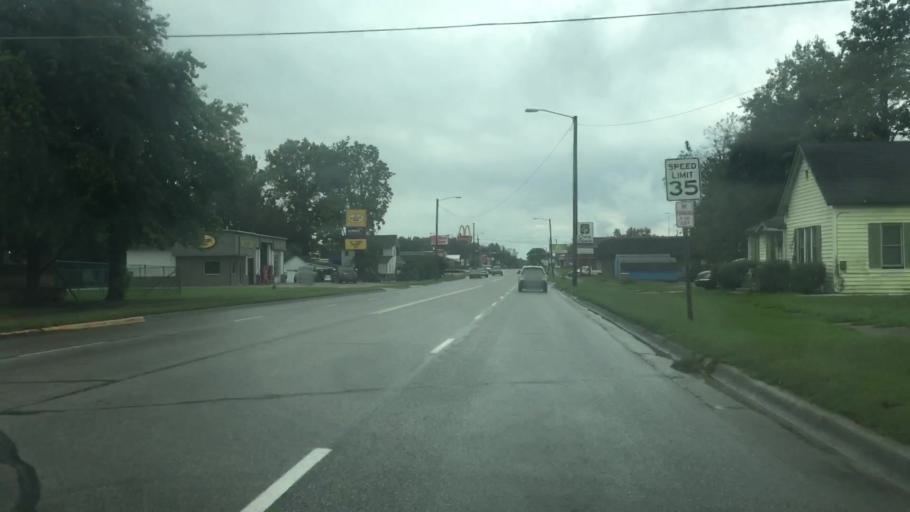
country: US
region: Kansas
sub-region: Allen County
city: Iola
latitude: 37.9246
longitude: -95.4091
